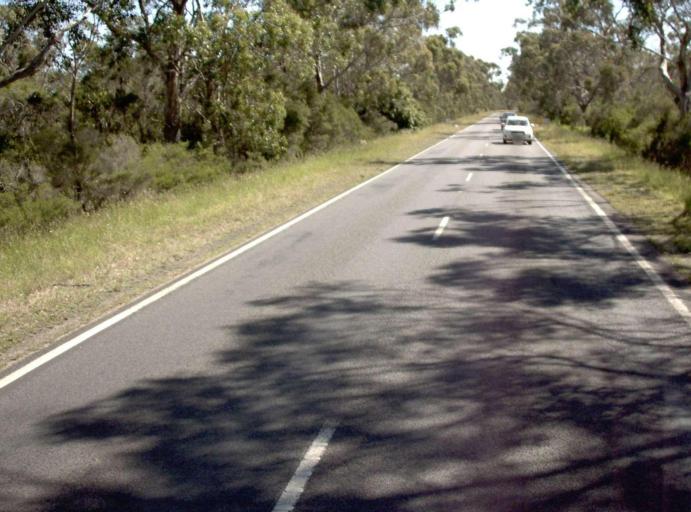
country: AU
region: Victoria
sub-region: Latrobe
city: Morwell
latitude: -38.6416
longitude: 146.5161
